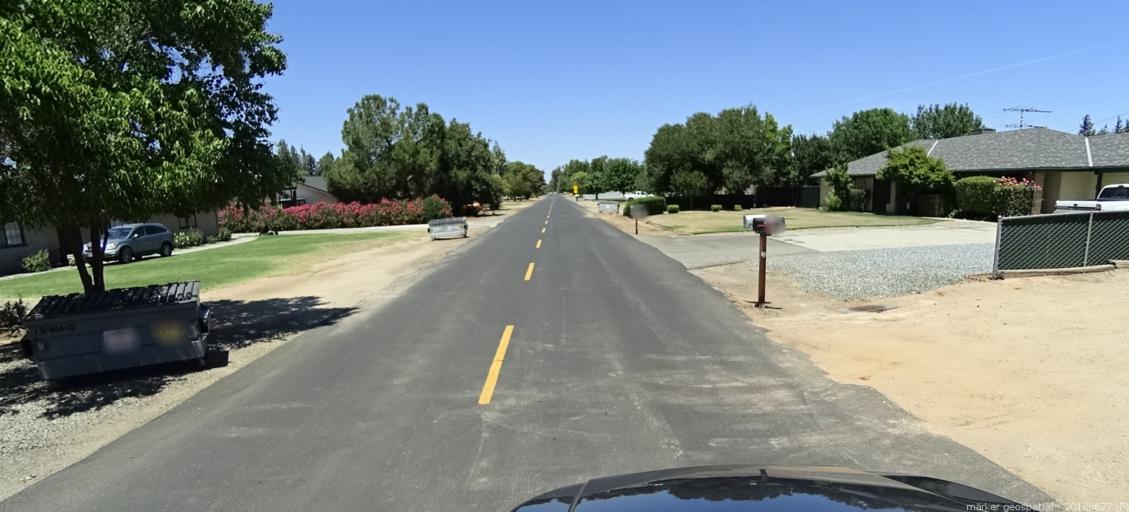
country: US
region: California
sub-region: Madera County
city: Bonadelle Ranchos-Madera Ranchos
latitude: 36.9255
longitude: -119.8809
